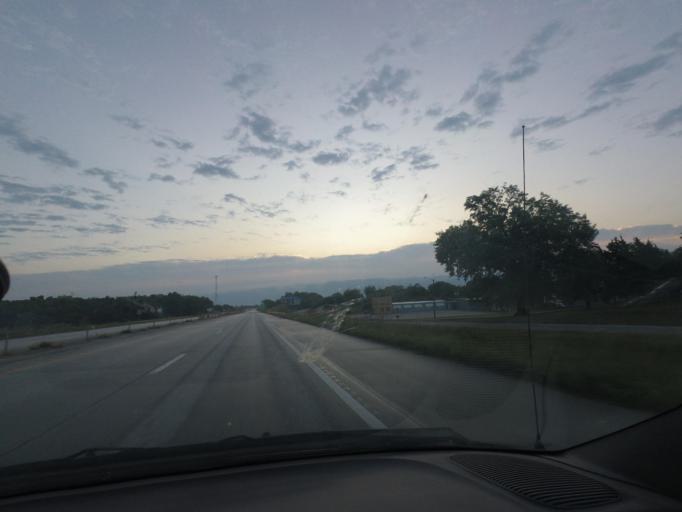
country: US
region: Missouri
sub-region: Macon County
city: Macon
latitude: 39.7512
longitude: -92.4760
